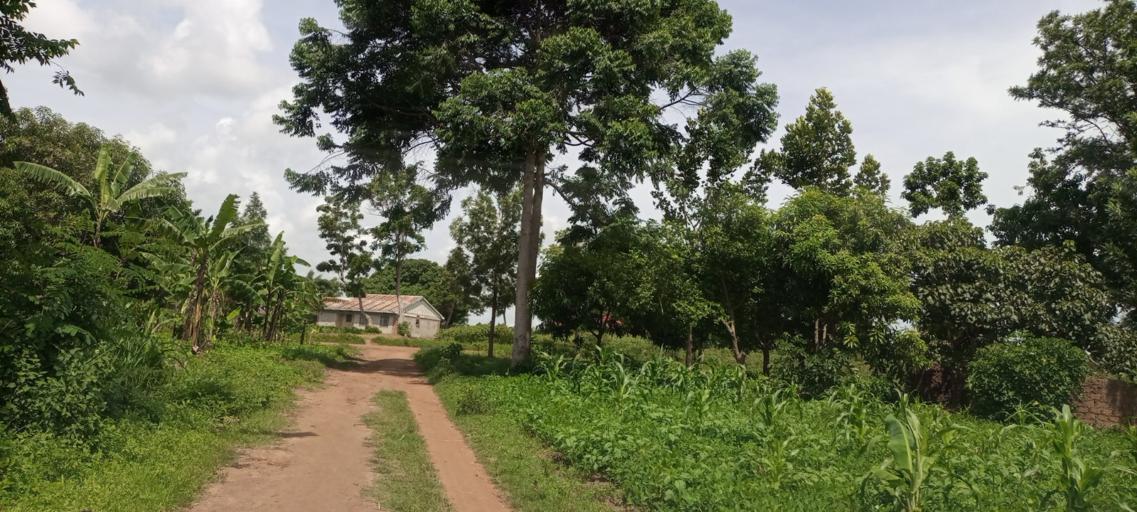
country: UG
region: Eastern Region
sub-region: Budaka District
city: Budaka
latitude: 1.1690
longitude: 33.9442
